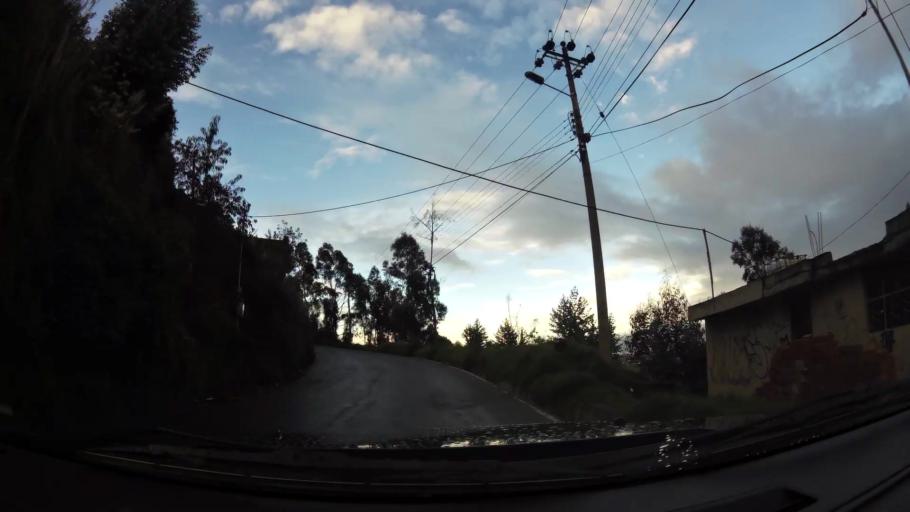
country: EC
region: Pichincha
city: Quito
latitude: -0.1179
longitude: -78.5150
